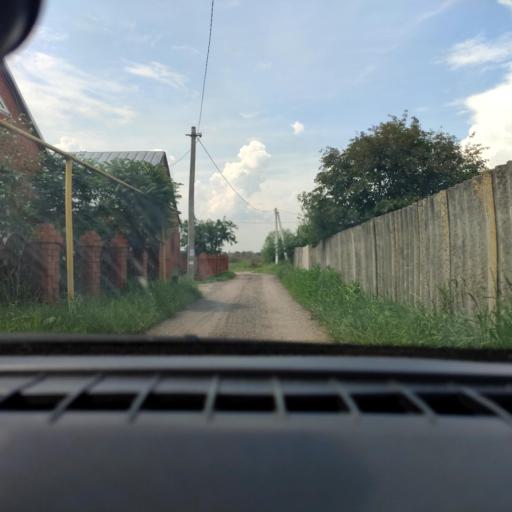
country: RU
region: Voronezj
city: Novaya Usman'
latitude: 51.6779
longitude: 39.3644
